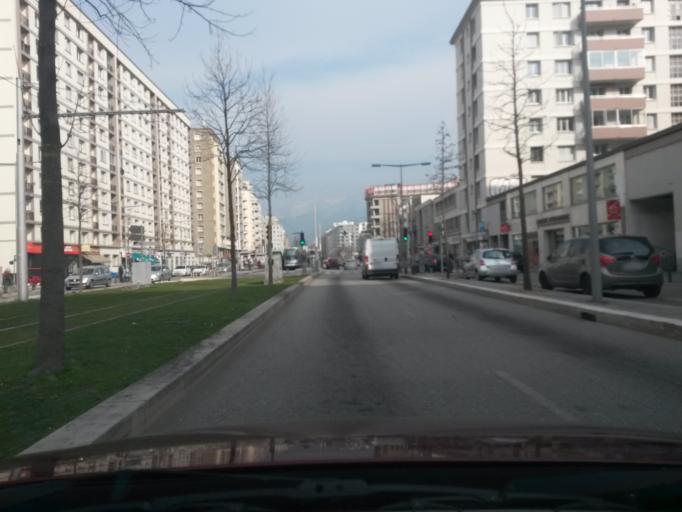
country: FR
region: Rhone-Alpes
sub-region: Departement de l'Isere
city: Grenoble
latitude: 45.1801
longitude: 5.7096
